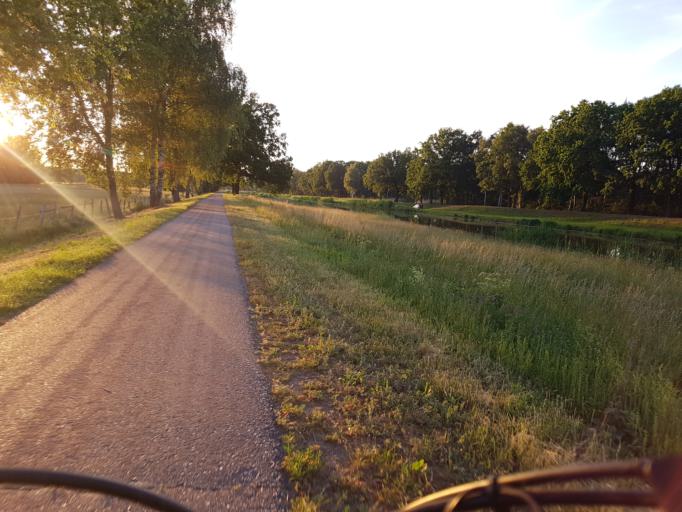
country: DE
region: Brandenburg
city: Schilda
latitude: 51.5778
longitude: 13.3445
